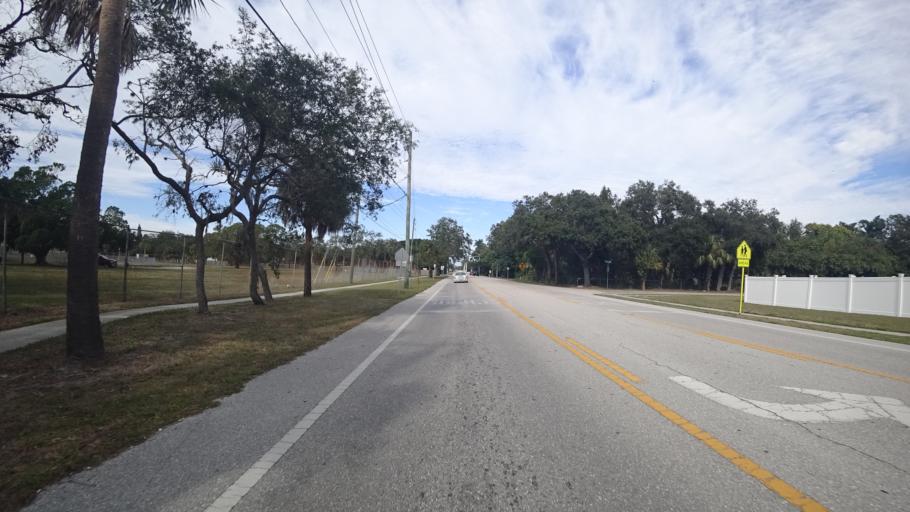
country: US
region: Florida
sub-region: Manatee County
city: West Bradenton
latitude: 27.5060
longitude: -82.6366
